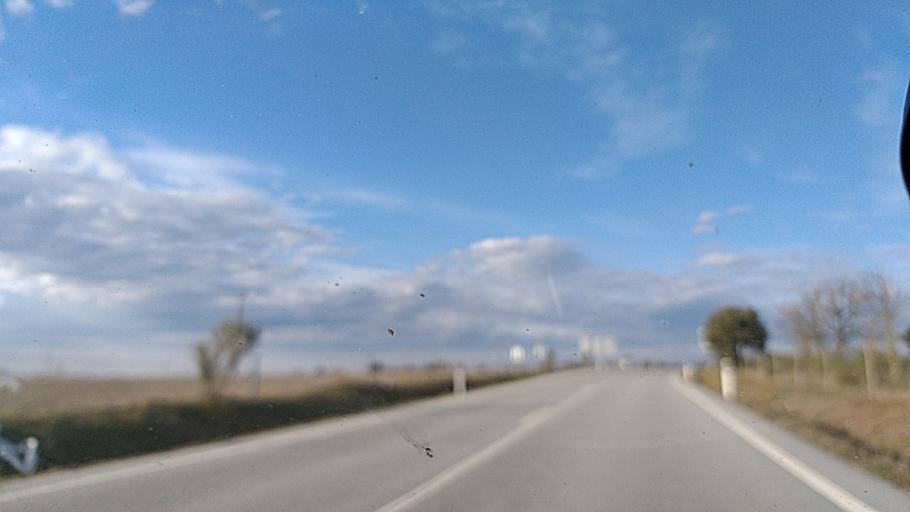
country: ES
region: Castille and Leon
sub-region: Provincia de Salamanca
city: Fuentes de Onoro
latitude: 40.6554
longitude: -6.8575
